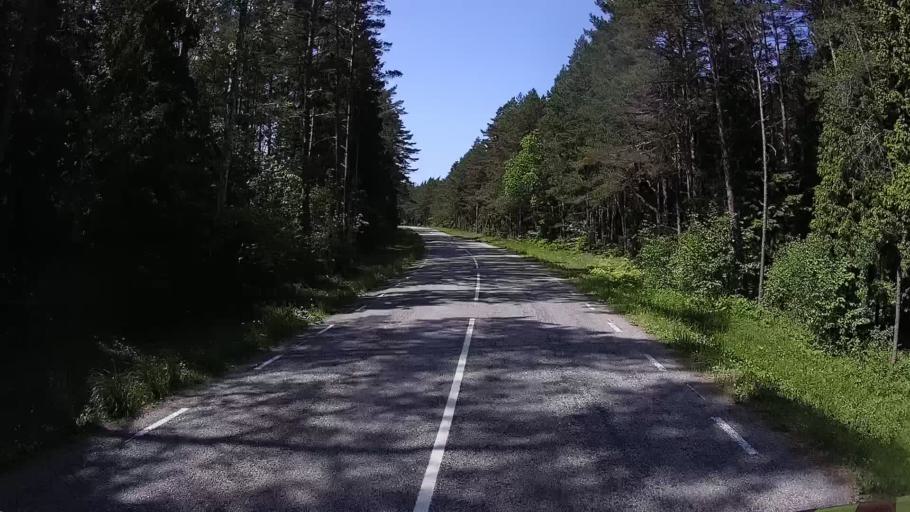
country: EE
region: Saare
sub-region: Kuressaare linn
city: Kuressaare
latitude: 57.9692
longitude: 22.1280
